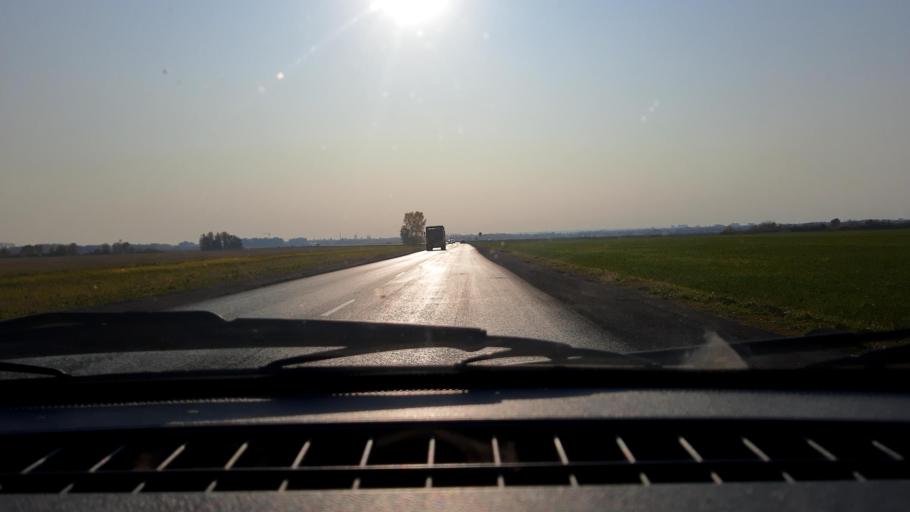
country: RU
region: Bashkortostan
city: Ufa
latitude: 54.8114
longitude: 55.9717
